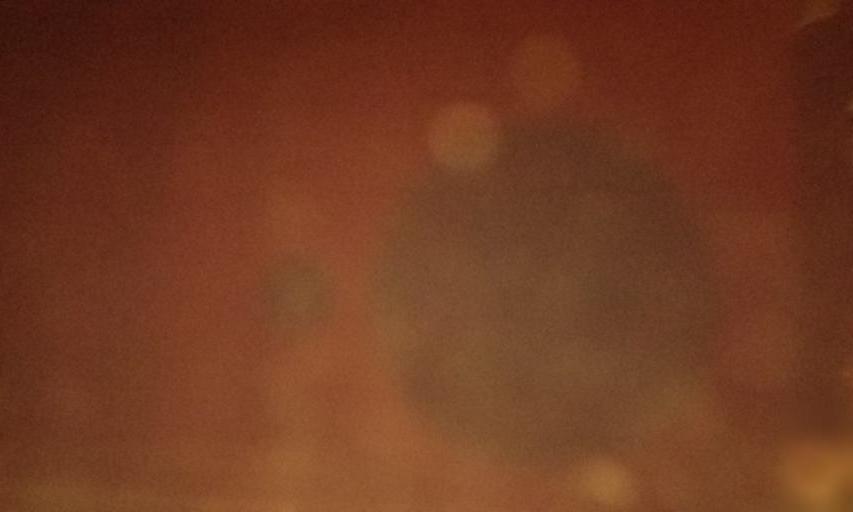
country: JP
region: Hyogo
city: Himeji
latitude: 34.8308
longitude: 134.6289
